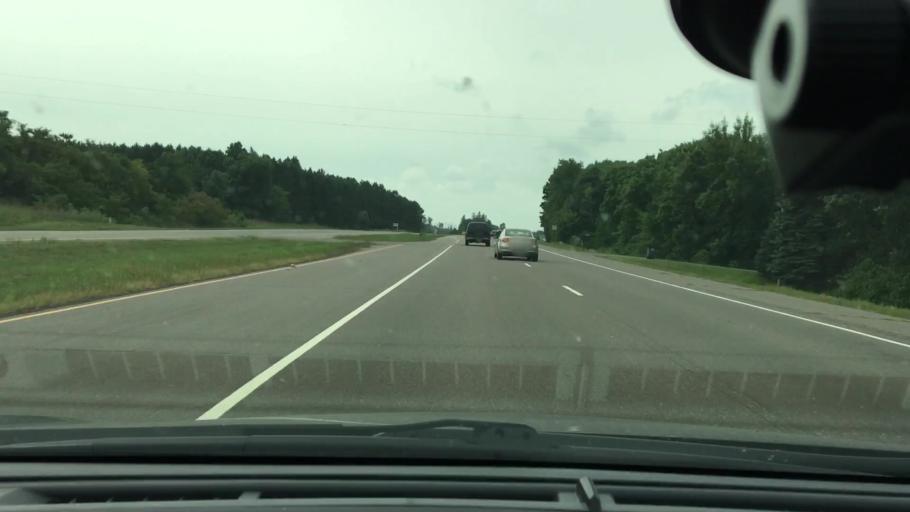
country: US
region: Minnesota
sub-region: Mille Lacs County
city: Vineland
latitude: 46.0808
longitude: -93.6517
